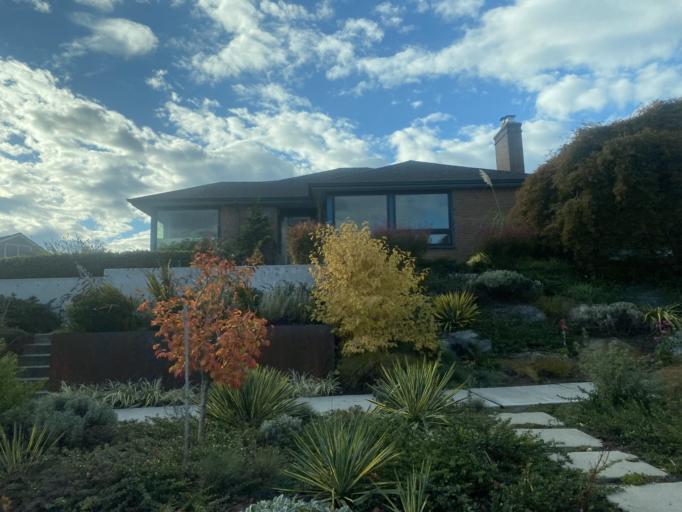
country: US
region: Washington
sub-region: King County
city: Seattle
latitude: 47.6361
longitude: -122.4012
